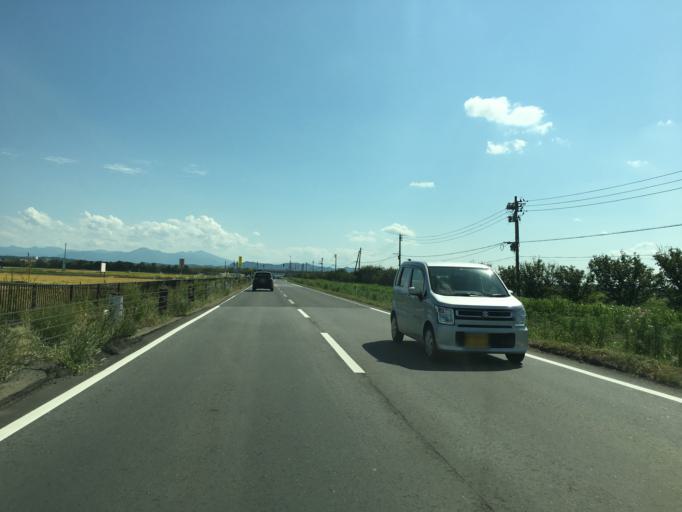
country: JP
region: Niigata
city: Niitsu-honcho
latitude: 37.8274
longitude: 139.0978
